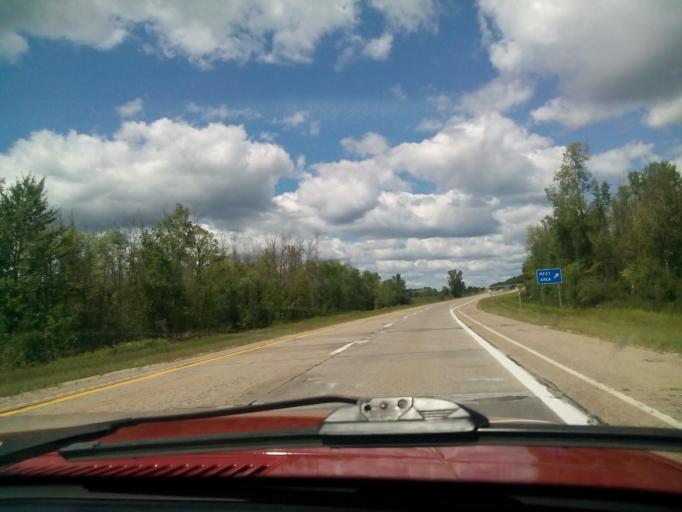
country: US
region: Michigan
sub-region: Ogemaw County
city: West Branch
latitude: 44.2233
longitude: -84.2087
